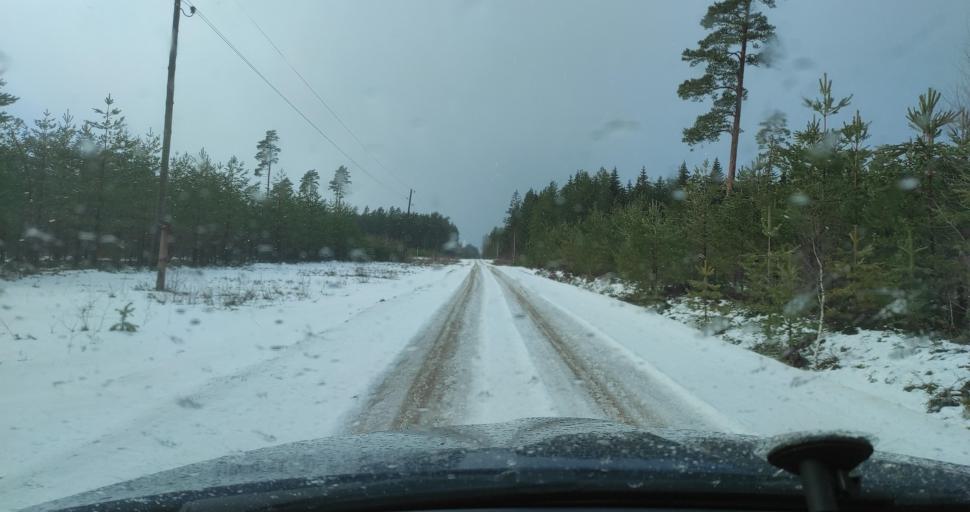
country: LV
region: Dundaga
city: Dundaga
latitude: 57.3830
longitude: 22.1508
